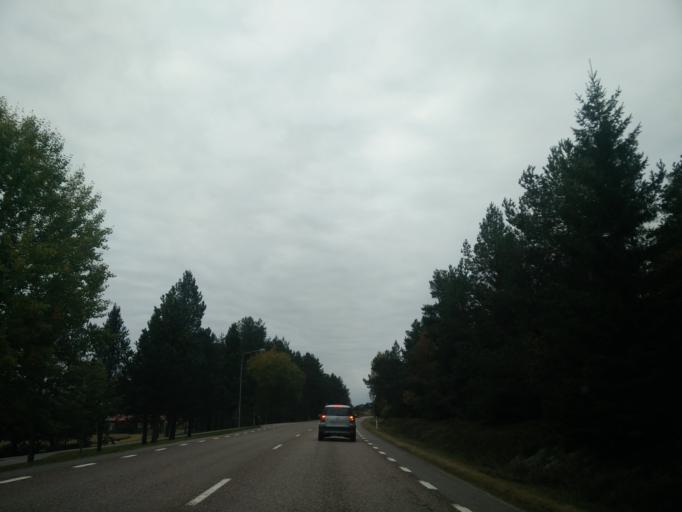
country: SE
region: Gaevleborg
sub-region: Gavle Kommun
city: Norrsundet
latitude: 60.8250
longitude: 17.2123
